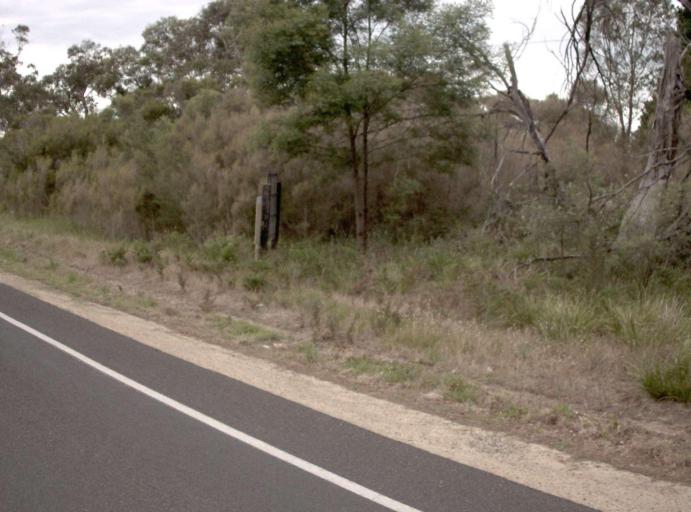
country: AU
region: Victoria
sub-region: Wellington
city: Sale
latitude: -38.2087
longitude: 147.0682
